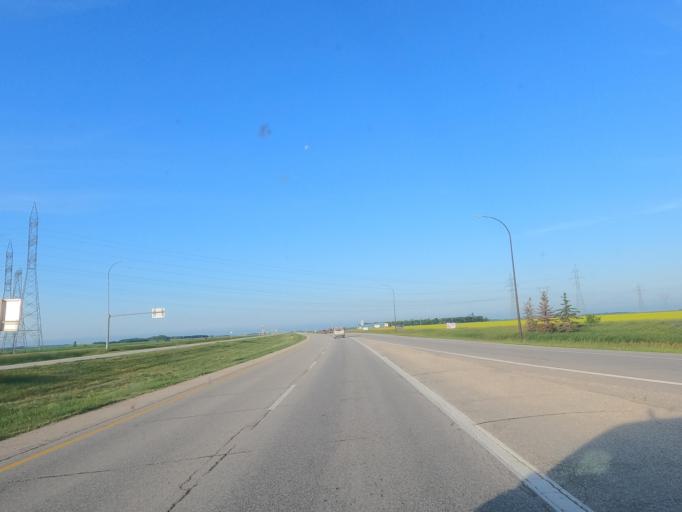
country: CA
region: Manitoba
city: Headingley
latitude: 49.9865
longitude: -97.3110
